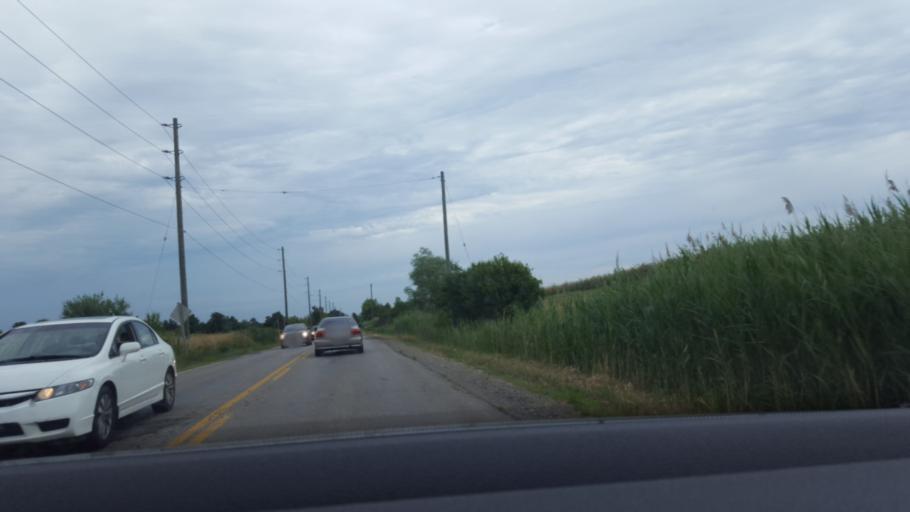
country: CA
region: Ontario
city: Brampton
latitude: 43.6190
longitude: -79.8343
